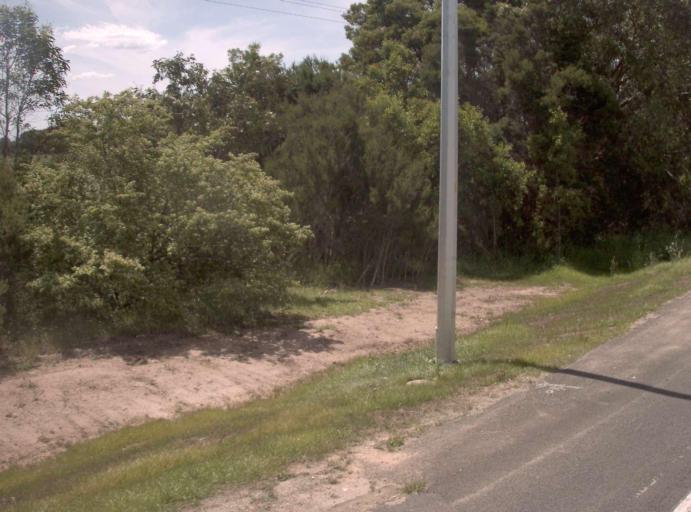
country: AU
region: Victoria
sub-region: Wellington
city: Sale
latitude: -38.0788
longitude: 147.0718
